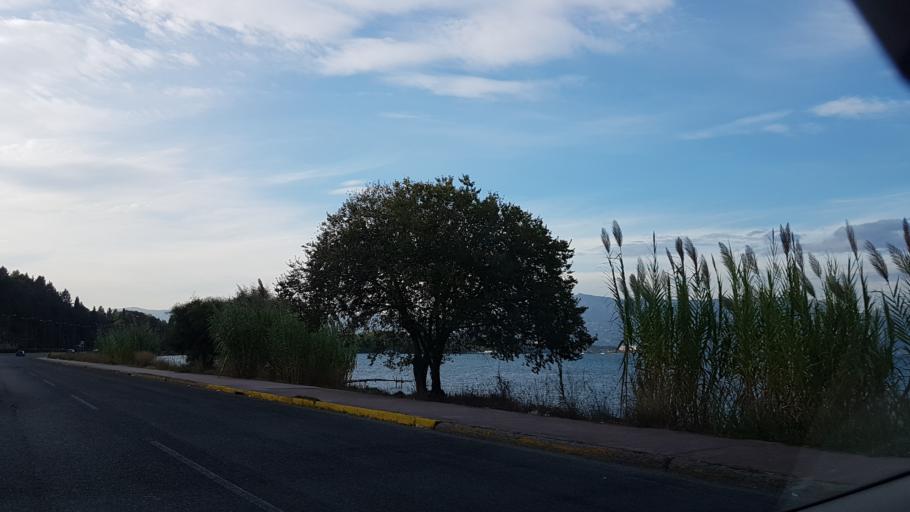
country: GR
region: Ionian Islands
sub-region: Nomos Kerkyras
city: Kontokali
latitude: 39.6395
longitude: 19.8660
